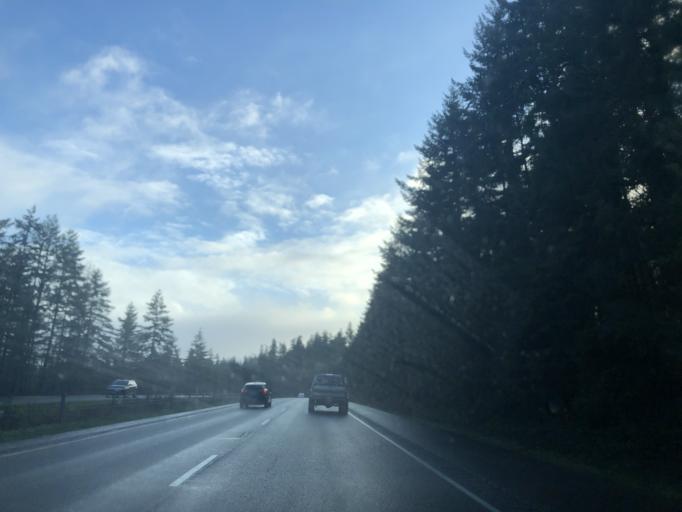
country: US
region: Washington
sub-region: Kitsap County
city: Erlands Point-Kitsap Lake
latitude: 47.5883
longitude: -122.6990
